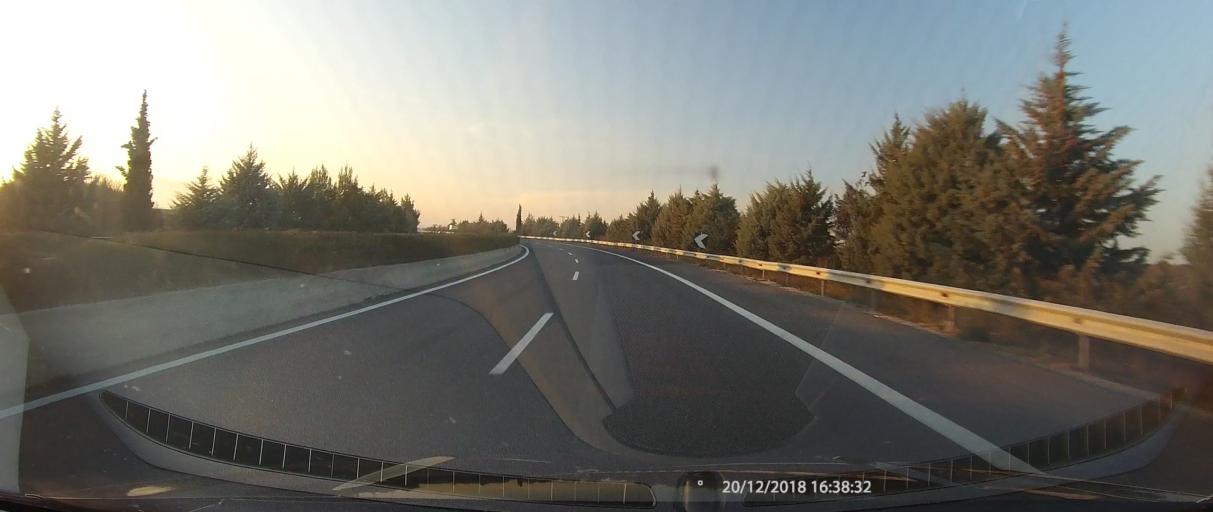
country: GR
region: Thessaly
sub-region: Nomos Magnisias
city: Velestino
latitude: 39.3460
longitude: 22.7812
